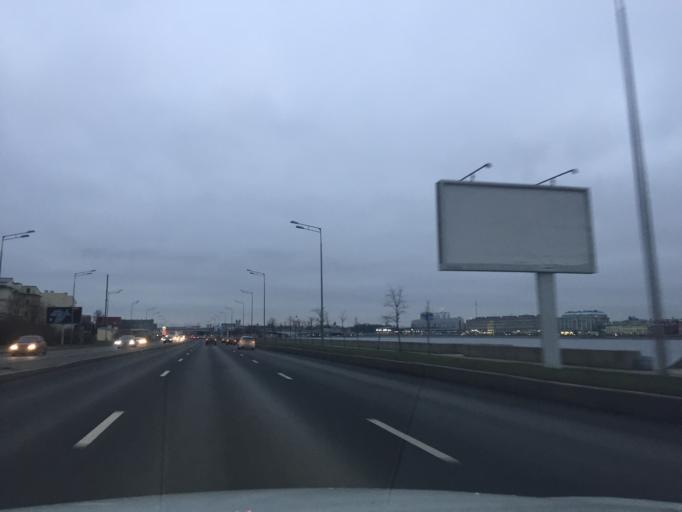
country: RU
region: St.-Petersburg
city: Centralniy
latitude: 59.9343
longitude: 30.4012
